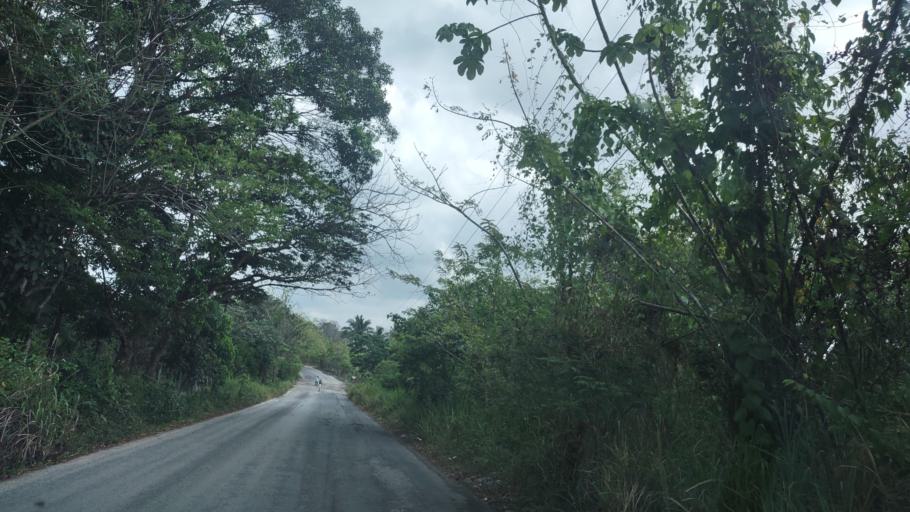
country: MX
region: Veracruz
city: Las Choapas
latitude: 17.9530
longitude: -94.1099
